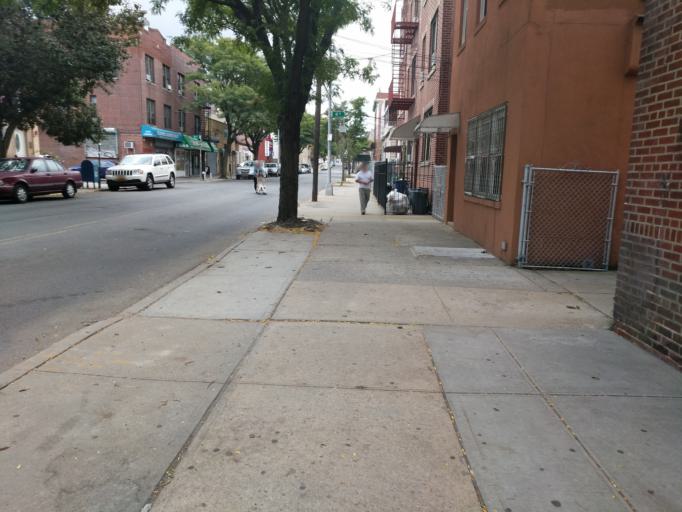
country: US
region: New York
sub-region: Queens County
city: Long Island City
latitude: 40.7445
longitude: -73.9069
